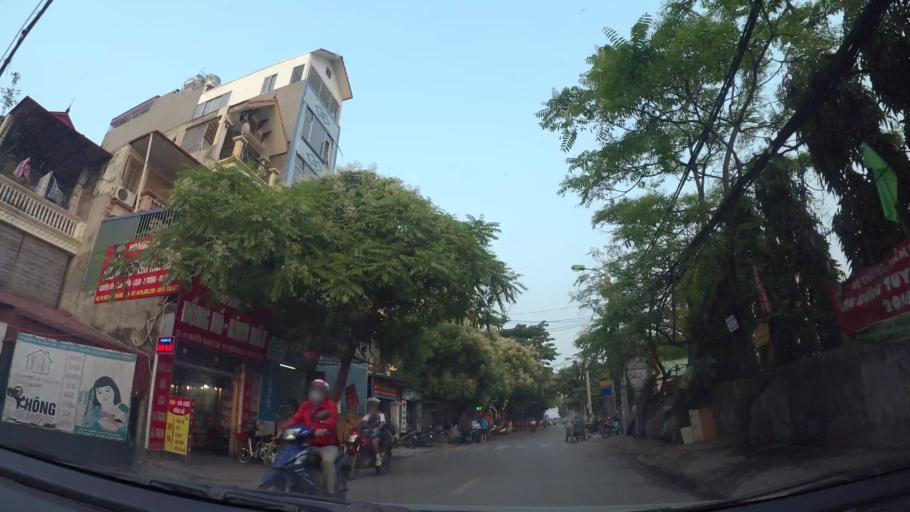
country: VN
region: Ha Noi
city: Tay Ho
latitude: 21.0714
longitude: 105.8065
